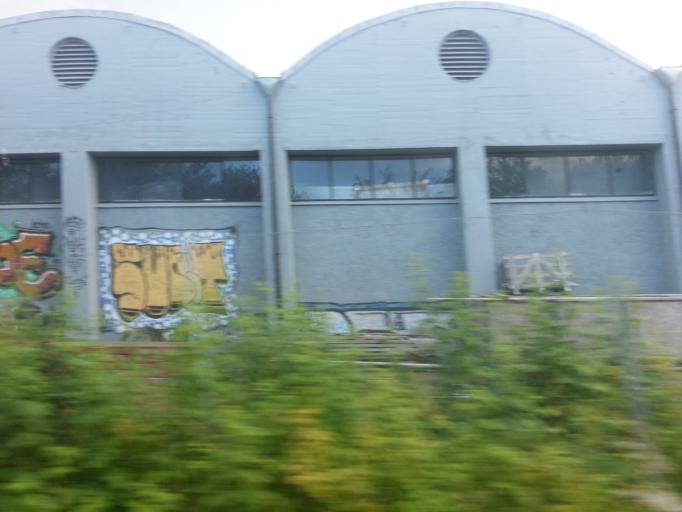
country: NO
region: Sor-Trondelag
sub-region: Trondheim
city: Trondheim
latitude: 63.4406
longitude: 10.4460
